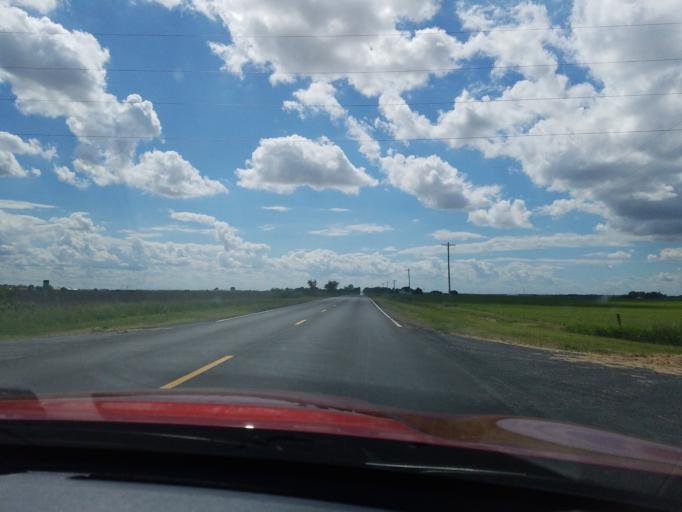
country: US
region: Nebraska
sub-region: Buffalo County
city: Kearney
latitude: 40.6410
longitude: -99.0657
